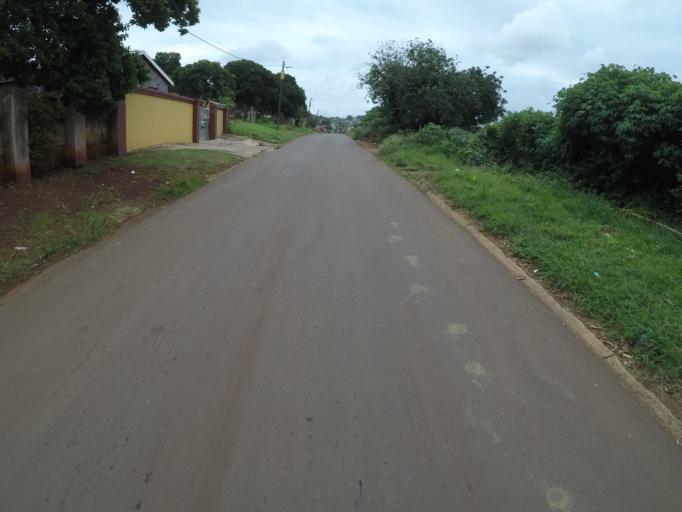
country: ZA
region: KwaZulu-Natal
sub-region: uThungulu District Municipality
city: Empangeni
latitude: -28.7665
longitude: 31.8624
